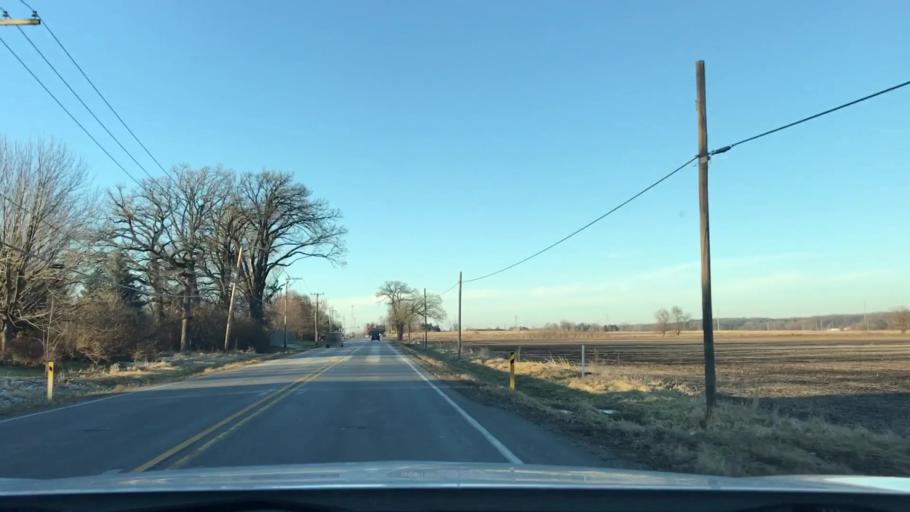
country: US
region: Illinois
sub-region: Kane County
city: Pingree Grove
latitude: 42.0931
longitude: -88.3996
